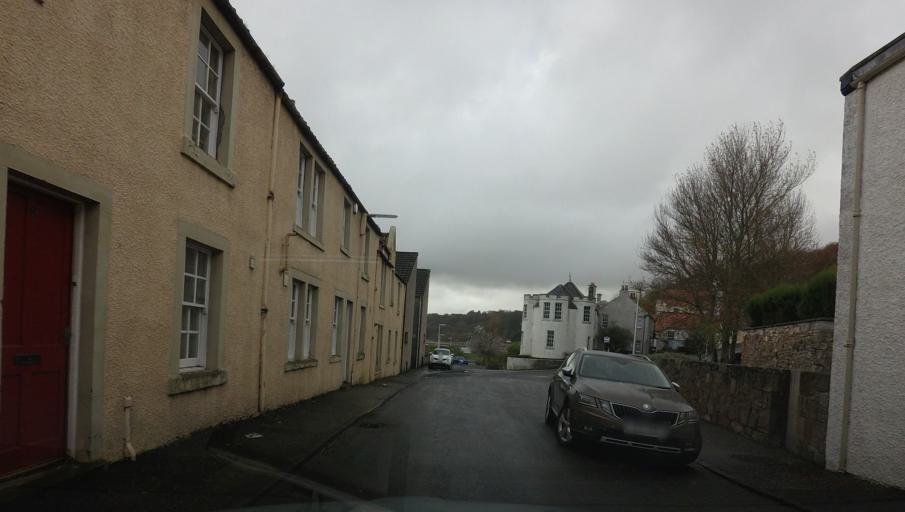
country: GB
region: Scotland
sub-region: Fife
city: East Wemyss
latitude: 56.1399
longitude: -3.0867
